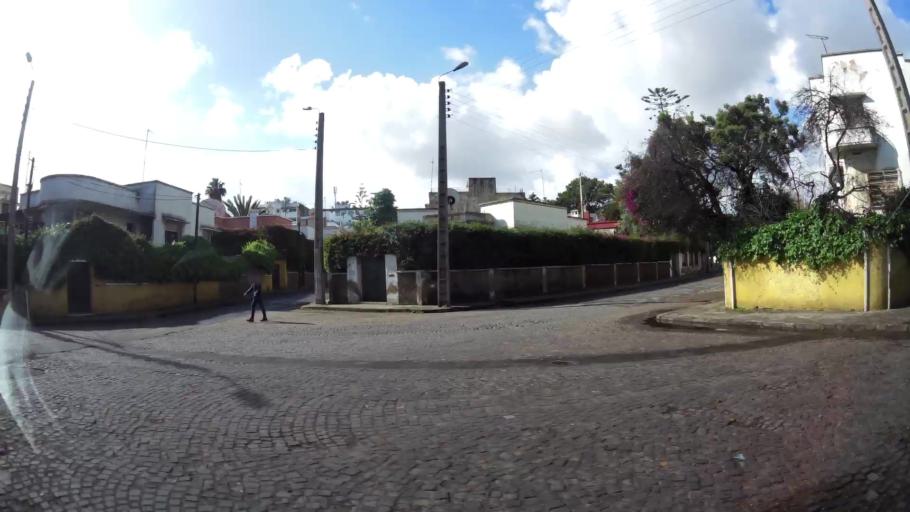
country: MA
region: Grand Casablanca
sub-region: Casablanca
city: Casablanca
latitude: 33.5809
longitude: -7.6296
